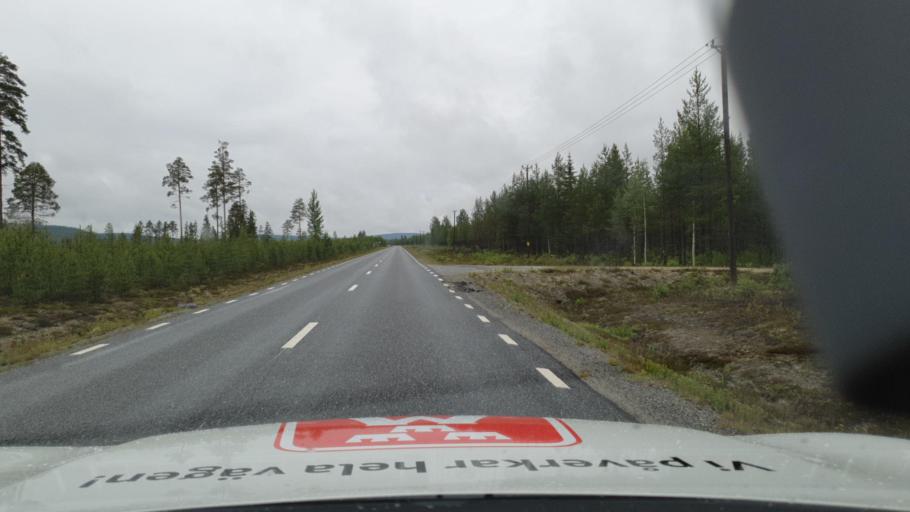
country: SE
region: Vaesterbotten
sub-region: Asele Kommun
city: Asele
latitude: 63.9522
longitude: 17.2729
